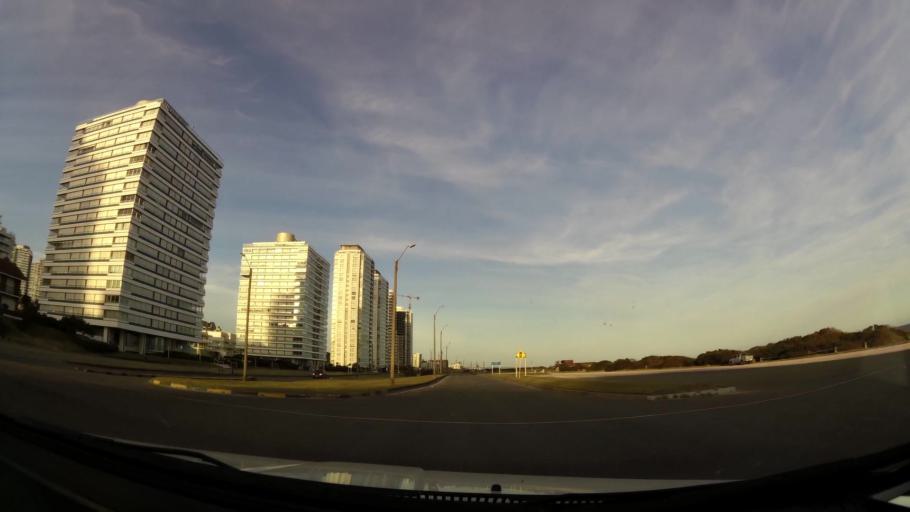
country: UY
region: Maldonado
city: Punta del Este
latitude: -34.9496
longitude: -54.9266
